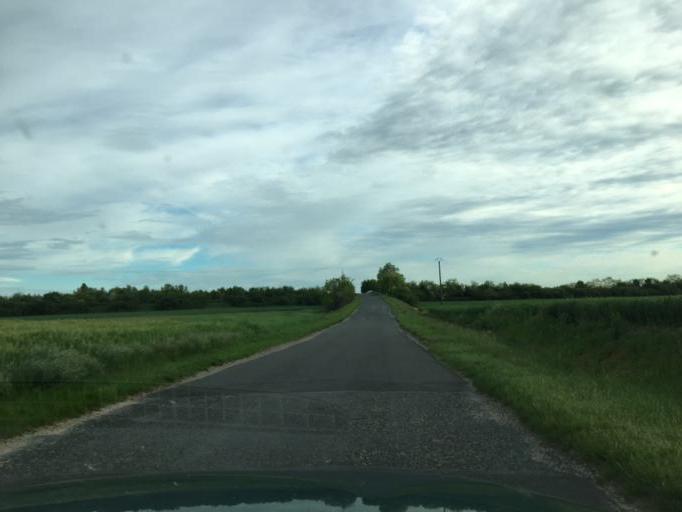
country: FR
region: Centre
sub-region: Departement du Loiret
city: La Chapelle-Saint-Mesmin
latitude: 47.8974
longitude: 1.8091
